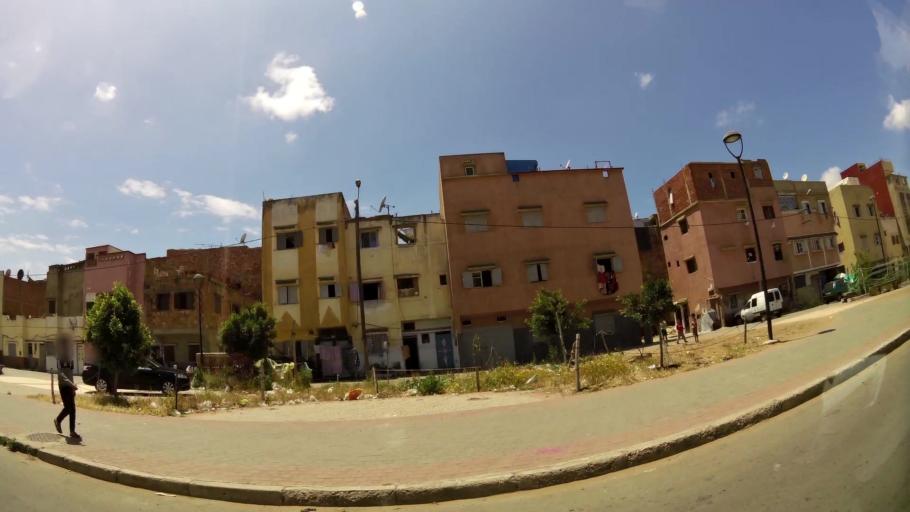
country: MA
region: Gharb-Chrarda-Beni Hssen
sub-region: Kenitra Province
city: Kenitra
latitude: 34.2620
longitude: -6.5564
